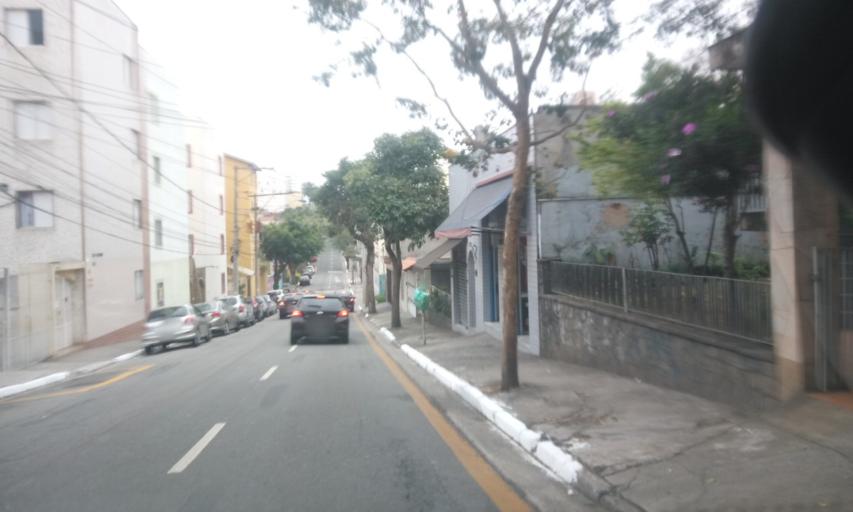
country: BR
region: Sao Paulo
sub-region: Sao Caetano Do Sul
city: Sao Caetano do Sul
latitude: -23.6266
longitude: -46.5693
